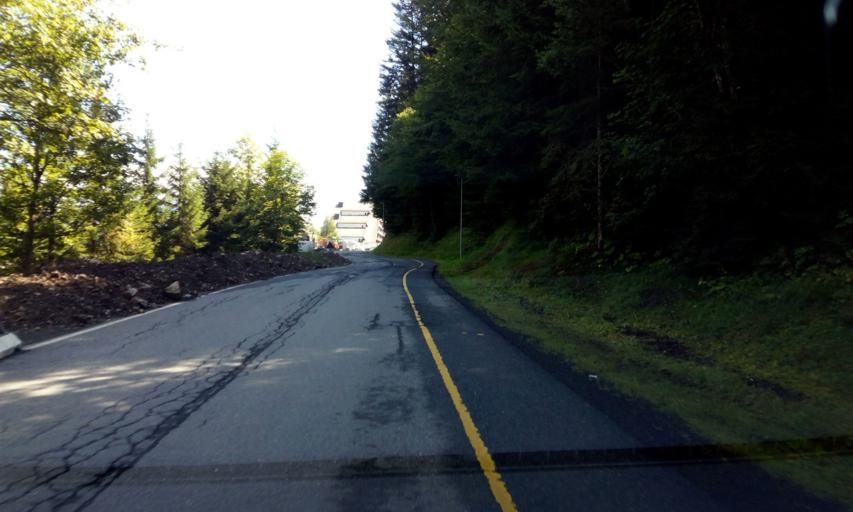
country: CH
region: Valais
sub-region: Monthey District
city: Vouvry
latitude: 46.3140
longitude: 6.8620
